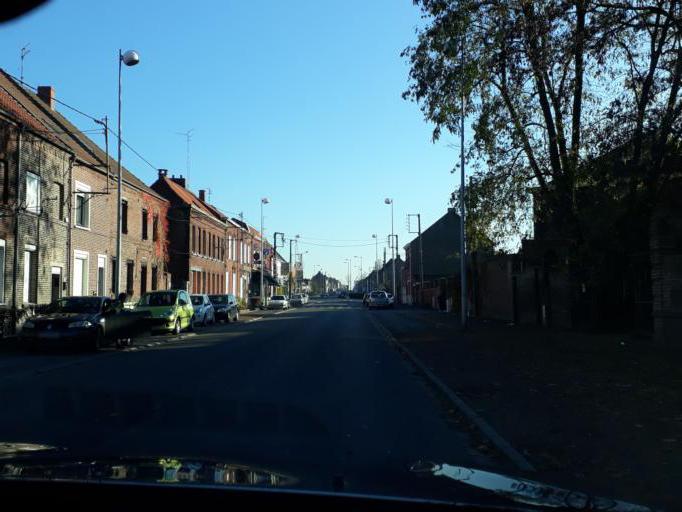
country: FR
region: Nord-Pas-de-Calais
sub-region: Departement du Nord
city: Auberchicourt
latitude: 50.3309
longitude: 3.2414
